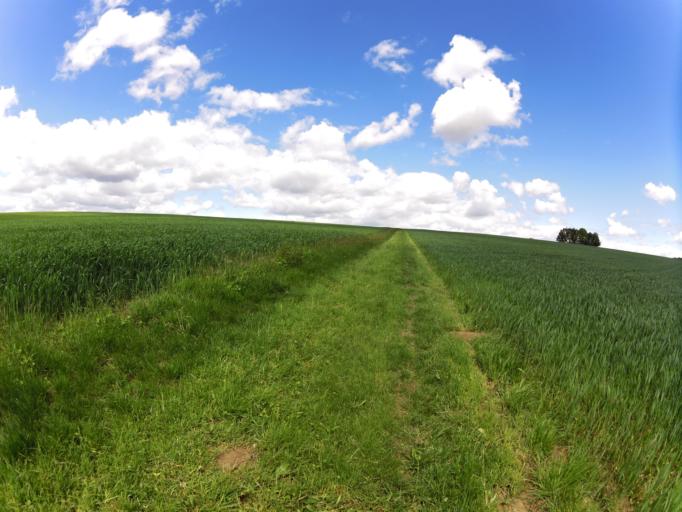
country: DE
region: Bavaria
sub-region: Regierungsbezirk Unterfranken
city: Volkach
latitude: 49.8751
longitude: 10.2456
